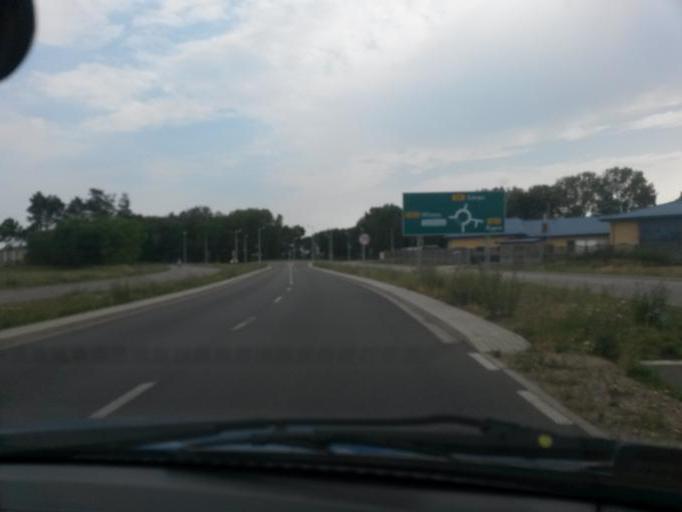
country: PL
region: Masovian Voivodeship
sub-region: Powiat zurominski
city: Zuromin
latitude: 53.0633
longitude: 19.8949
